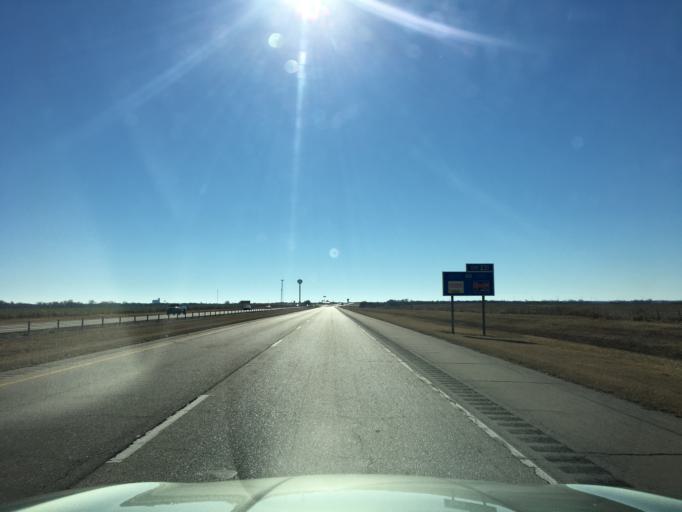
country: US
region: Oklahoma
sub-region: Kay County
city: Blackwell
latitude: 36.9546
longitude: -97.3458
